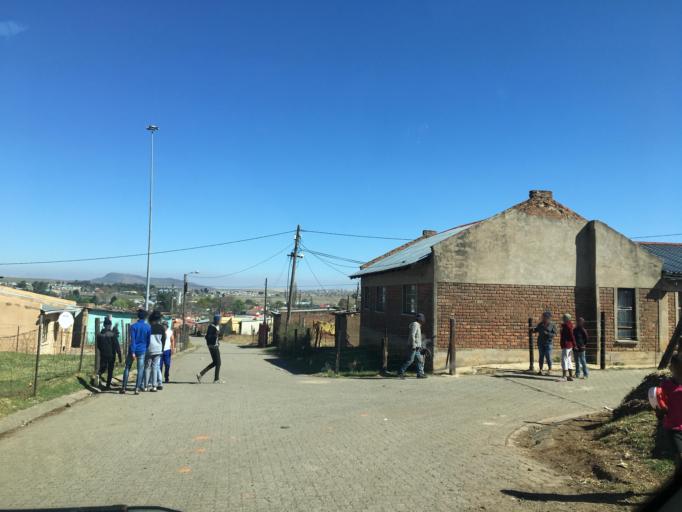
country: ZA
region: Eastern Cape
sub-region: Chris Hani District Municipality
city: Elliot
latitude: -31.3378
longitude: 27.8569
